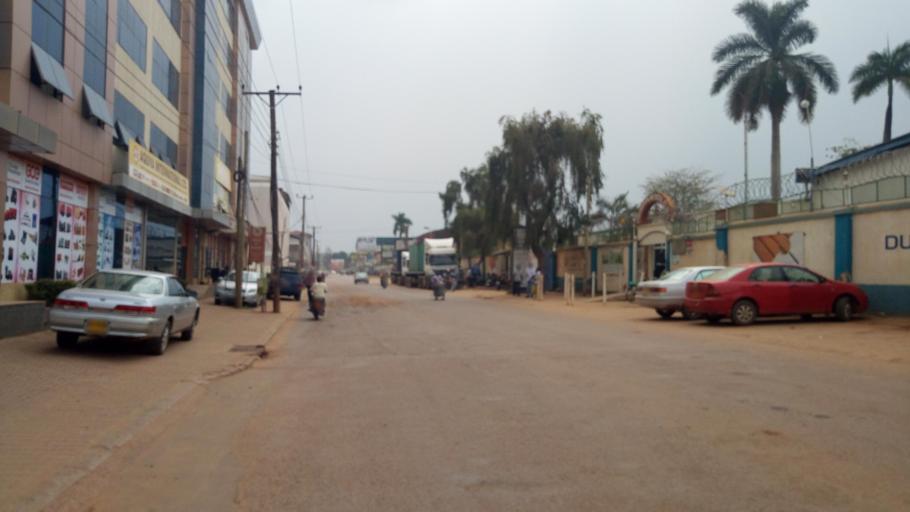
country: UG
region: Central Region
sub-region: Kampala District
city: Kampala
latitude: 0.3140
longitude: 32.6151
